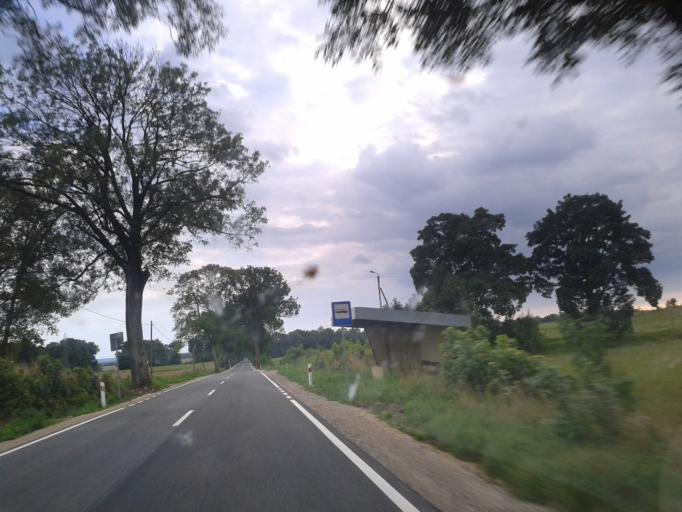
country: PL
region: West Pomeranian Voivodeship
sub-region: Powiat szczecinecki
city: Grzmiaca
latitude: 53.8652
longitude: 16.4819
